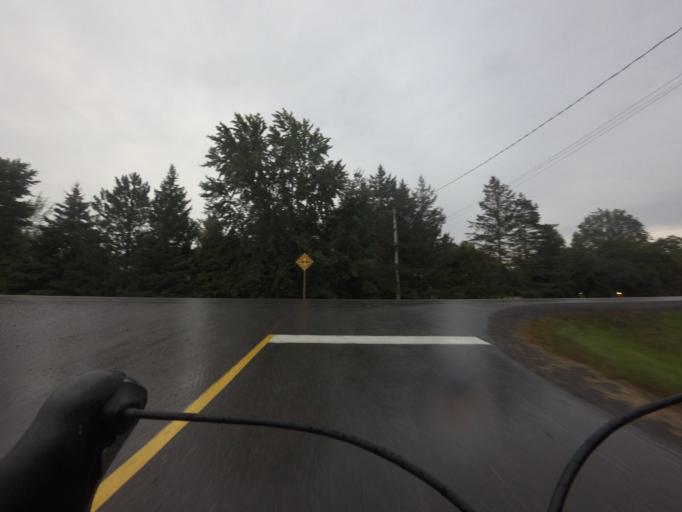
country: CA
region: Ontario
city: Bells Corners
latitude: 45.1896
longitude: -75.6804
